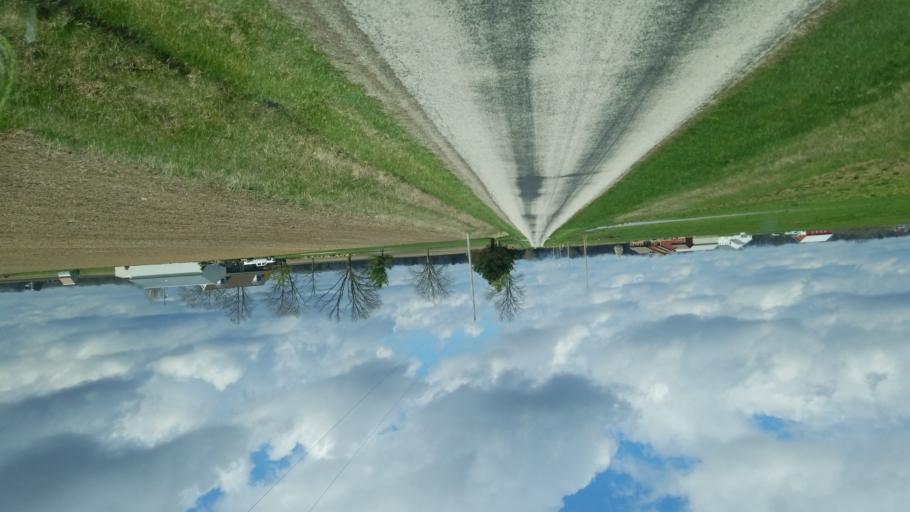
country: US
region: Ohio
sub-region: Union County
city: Richwood
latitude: 40.3552
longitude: -83.2379
